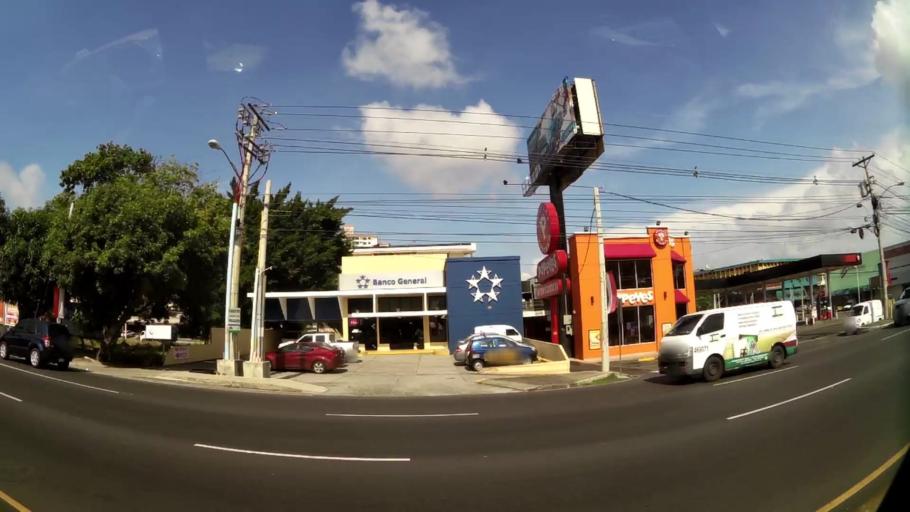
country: PA
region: Panama
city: Panama
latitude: 8.9977
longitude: -79.5266
